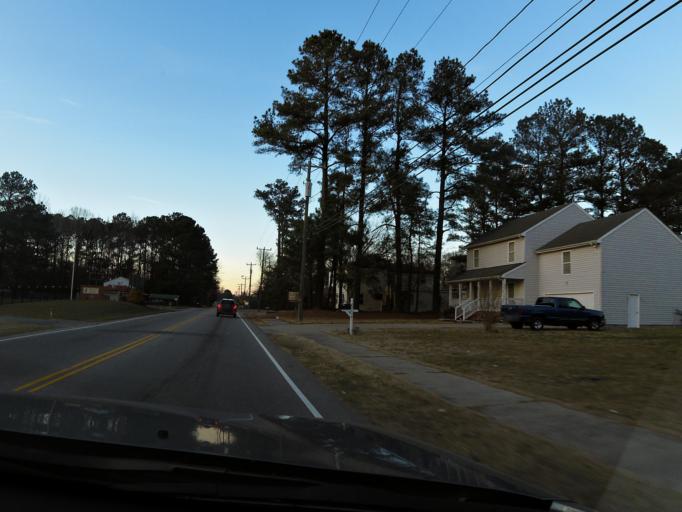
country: US
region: Virginia
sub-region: Southampton County
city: Courtland
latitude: 36.7244
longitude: -77.0710
